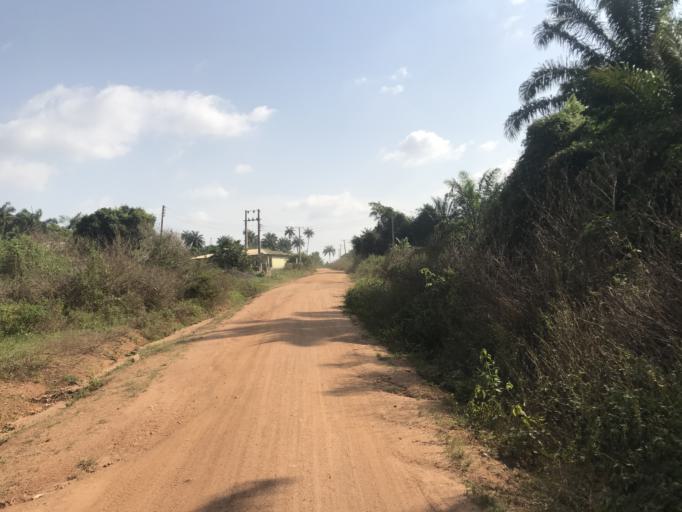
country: NG
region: Osun
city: Ikirun
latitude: 7.8627
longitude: 4.5879
